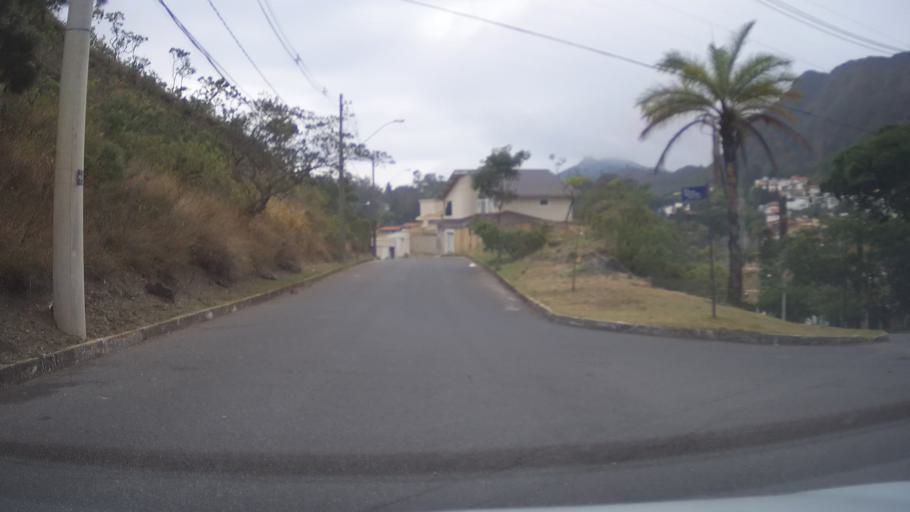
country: BR
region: Minas Gerais
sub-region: Belo Horizonte
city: Belo Horizonte
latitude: -19.9583
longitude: -43.9170
